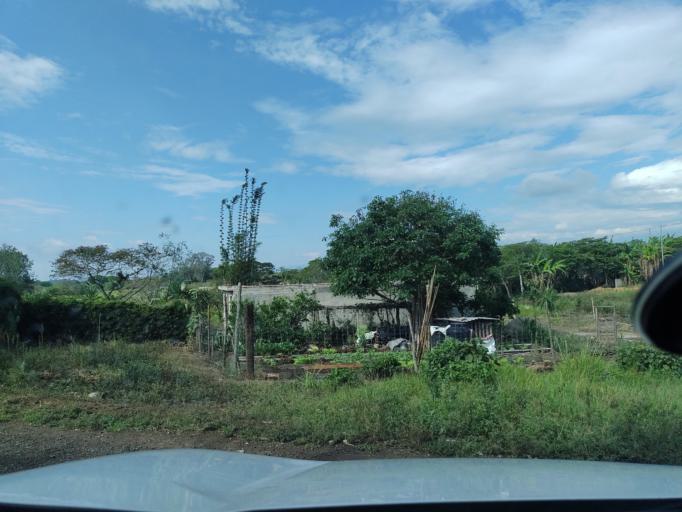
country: MX
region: Veracruz
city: Coatepec
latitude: 19.4812
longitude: -96.9311
